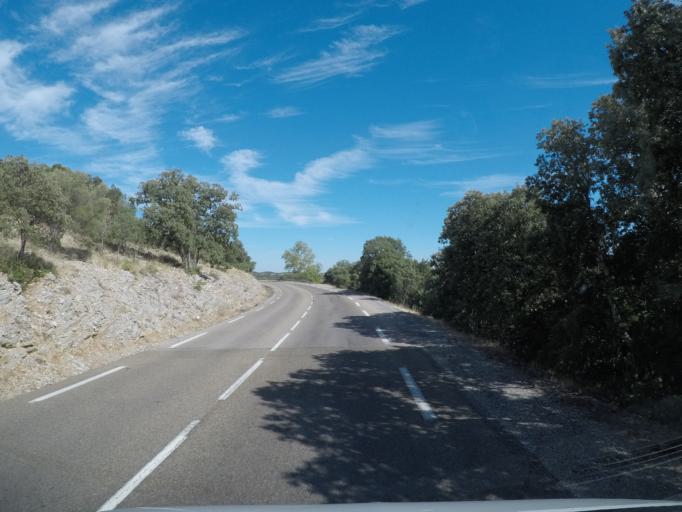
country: FR
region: Languedoc-Roussillon
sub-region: Departement du Gard
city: Sauve
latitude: 43.9603
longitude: 3.9072
